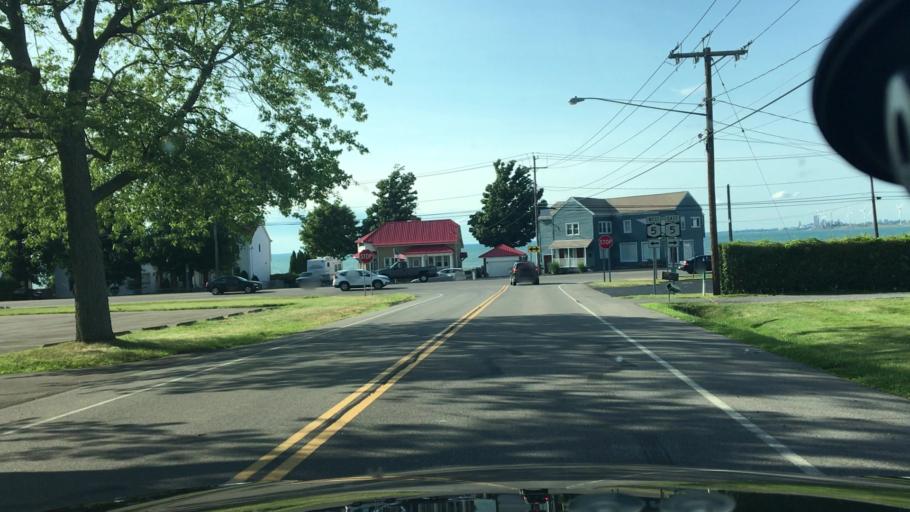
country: US
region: New York
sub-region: Erie County
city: Wanakah
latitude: 42.7694
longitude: -78.8669
